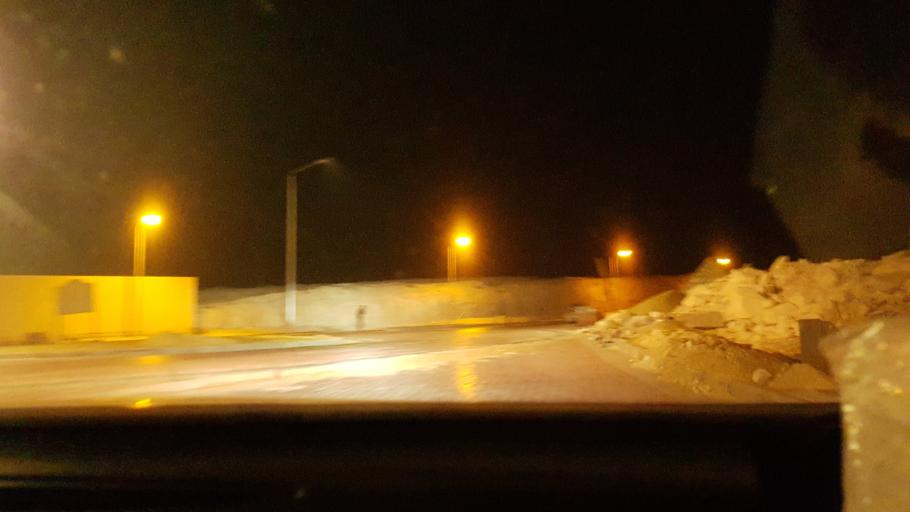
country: EG
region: Muhafazat Matruh
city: Al `Alamayn
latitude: 31.0637
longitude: 28.3614
